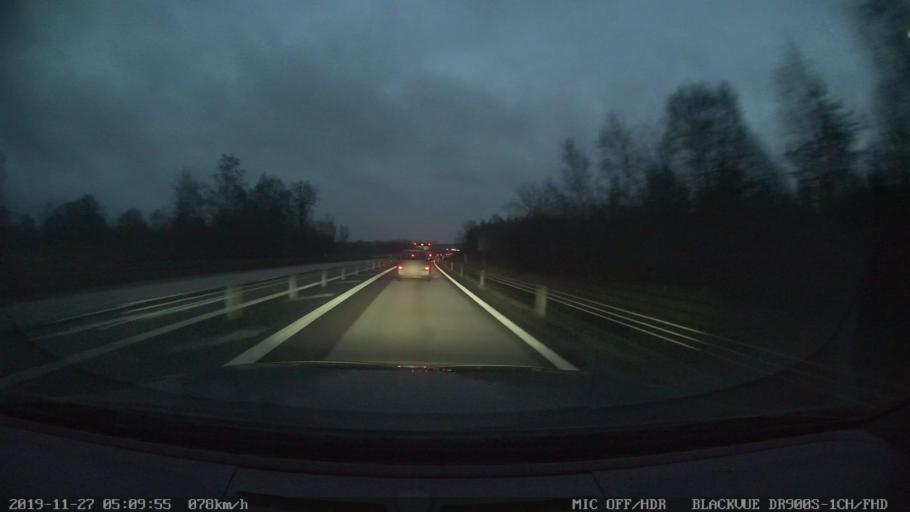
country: SE
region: Skane
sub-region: Helsingborg
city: Helsingborg
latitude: 56.1060
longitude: 12.6591
